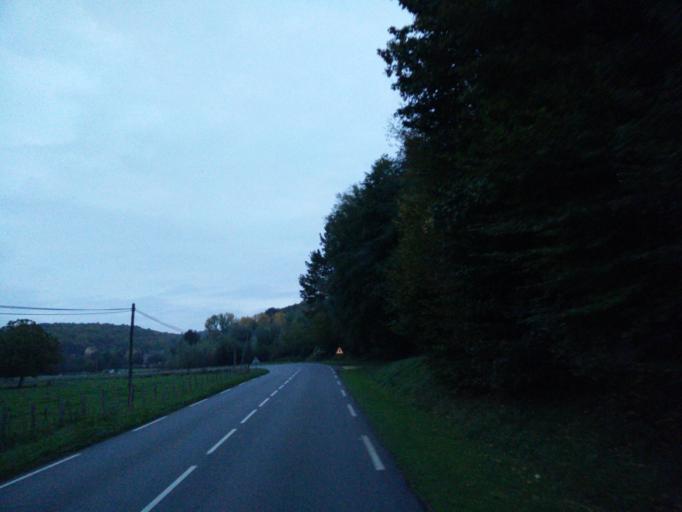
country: FR
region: Aquitaine
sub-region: Departement de la Dordogne
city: Saint-Cyprien
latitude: 44.9074
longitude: 1.1160
